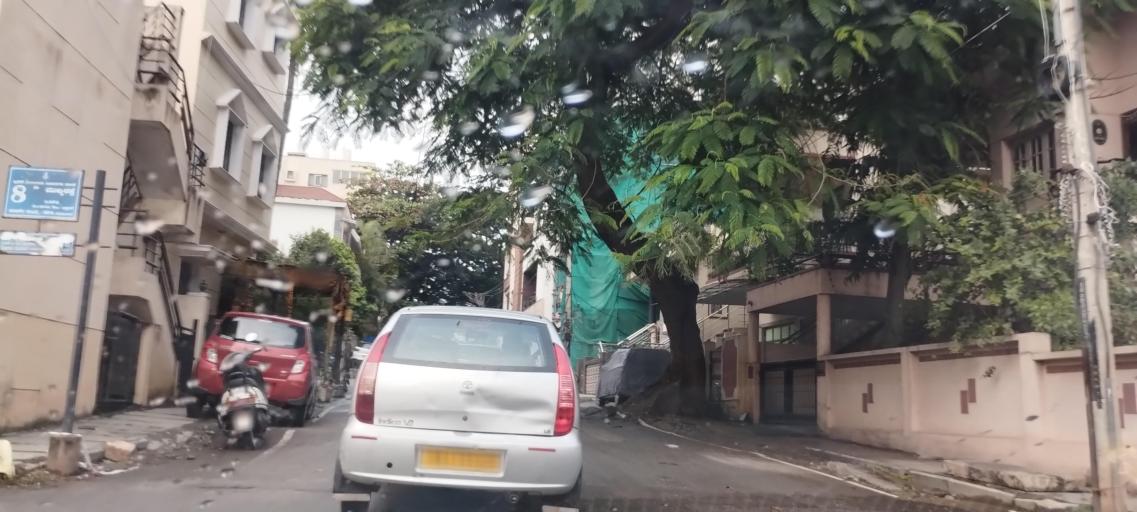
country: IN
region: Karnataka
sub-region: Bangalore Urban
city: Bangalore
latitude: 12.9391
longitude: 77.5614
